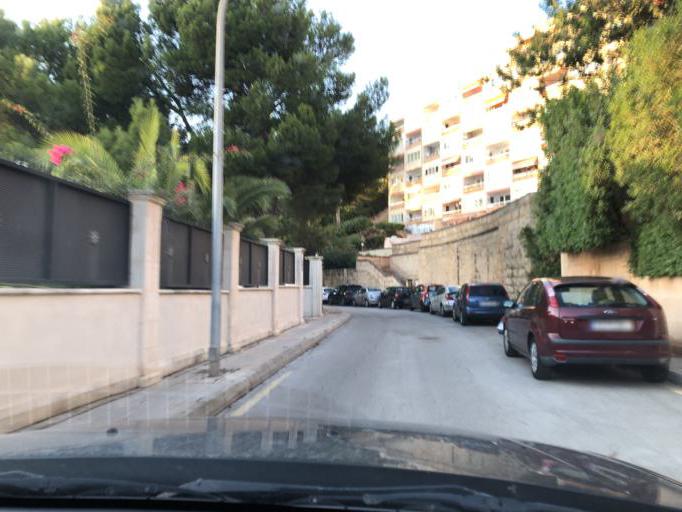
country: ES
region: Balearic Islands
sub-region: Illes Balears
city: Santa Ponsa
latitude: 39.5268
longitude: 2.4646
